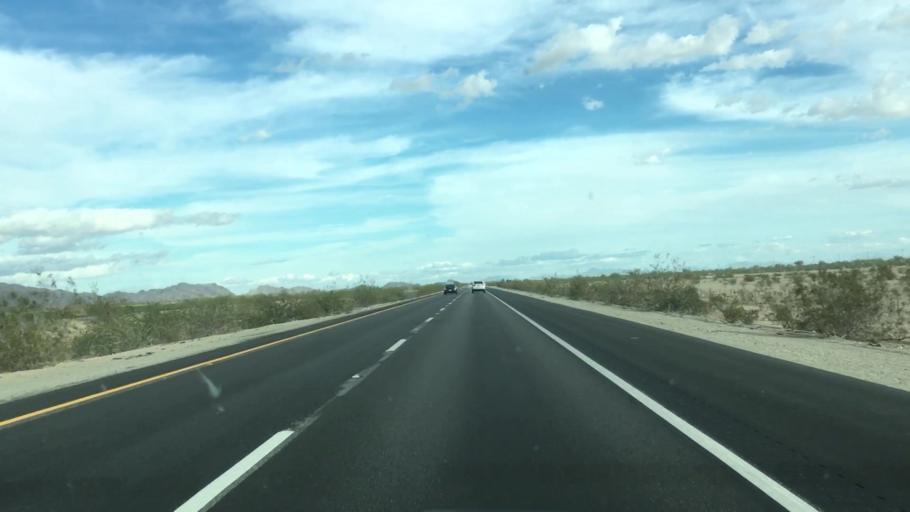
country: US
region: California
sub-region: Riverside County
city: Mesa Verde
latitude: 33.6090
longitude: -114.8609
